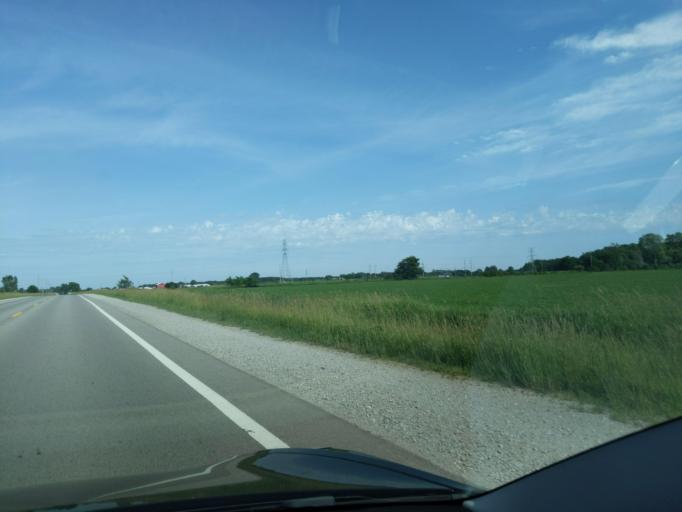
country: US
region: Michigan
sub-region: Newaygo County
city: Fremont
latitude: 43.4242
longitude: -86.0562
